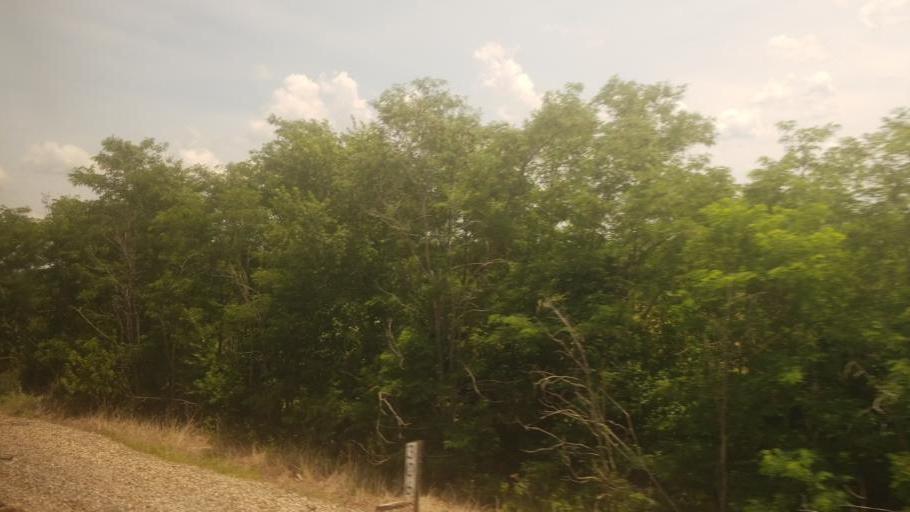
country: US
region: Missouri
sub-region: Macon County
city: La Plata
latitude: 40.0989
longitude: -92.4121
